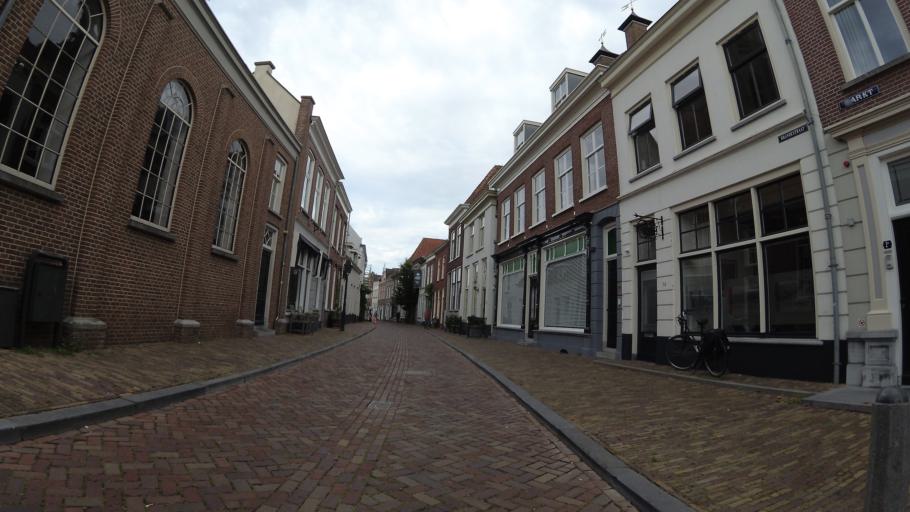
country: NL
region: North Brabant
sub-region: Gemeente Geertruidenberg
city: Geertruidenberg
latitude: 51.7004
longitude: 4.8619
